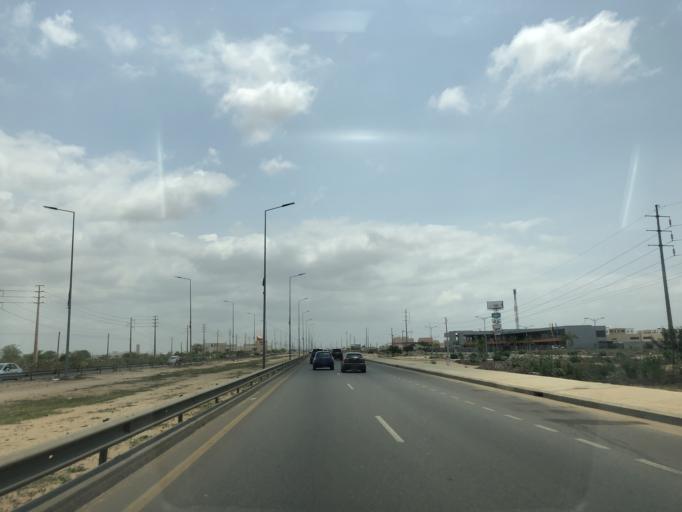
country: AO
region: Luanda
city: Luanda
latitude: -8.9519
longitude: 13.2588
